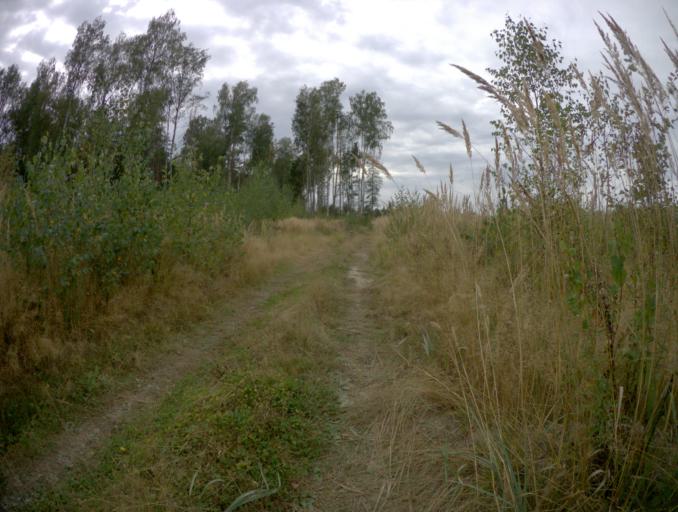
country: RU
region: Vladimir
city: Urshel'skiy
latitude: 55.8151
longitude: 40.2514
